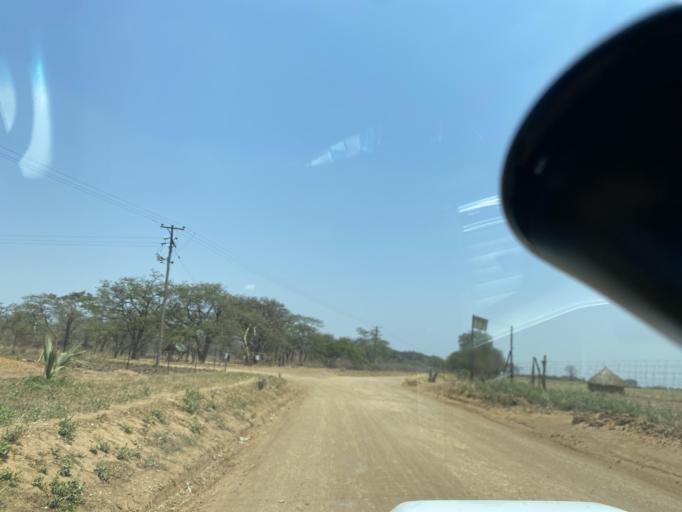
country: ZM
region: Lusaka
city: Lusaka
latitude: -15.4335
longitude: 28.0806
